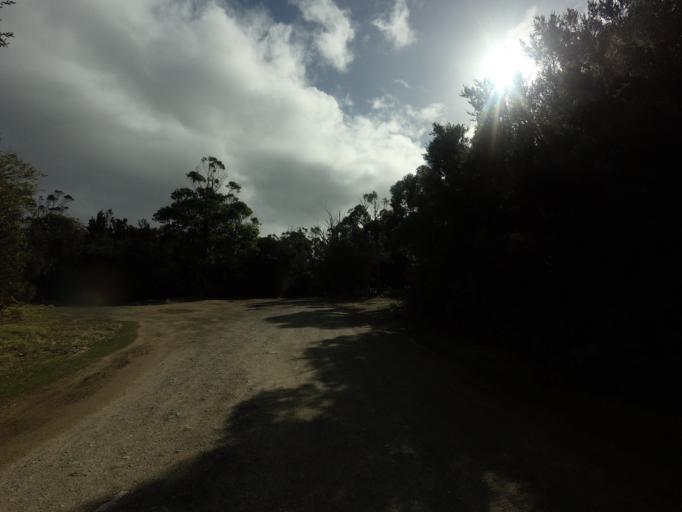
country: AU
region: Tasmania
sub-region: Huon Valley
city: Geeveston
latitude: -43.5787
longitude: 146.9010
